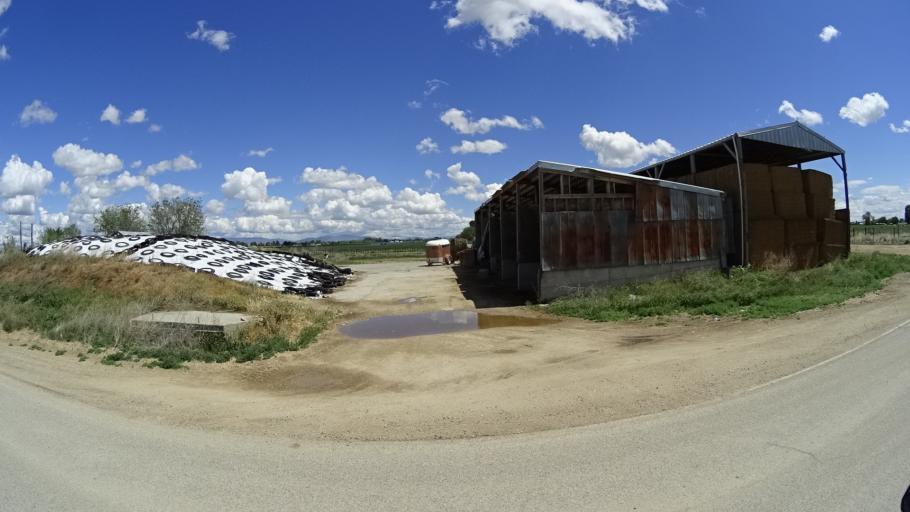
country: US
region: Idaho
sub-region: Ada County
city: Kuna
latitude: 43.5507
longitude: -116.4537
